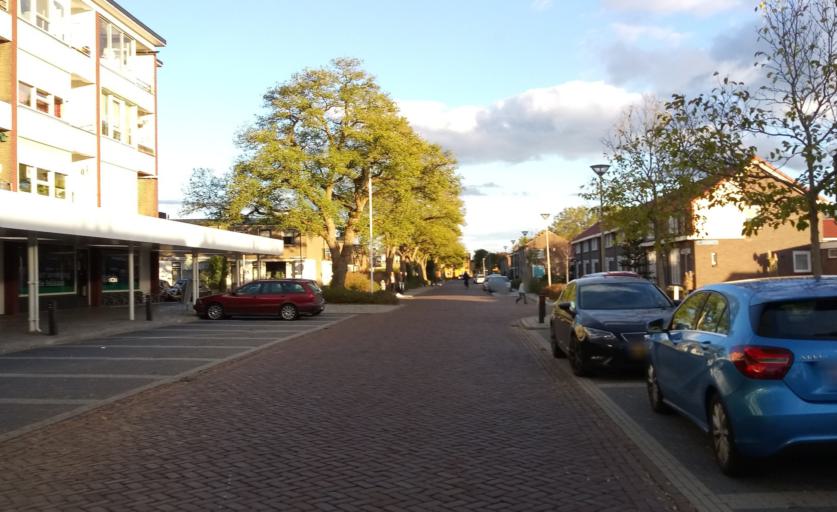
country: NL
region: Gelderland
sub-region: Gemeente Zutphen
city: Zutphen
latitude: 52.1323
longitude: 6.2052
